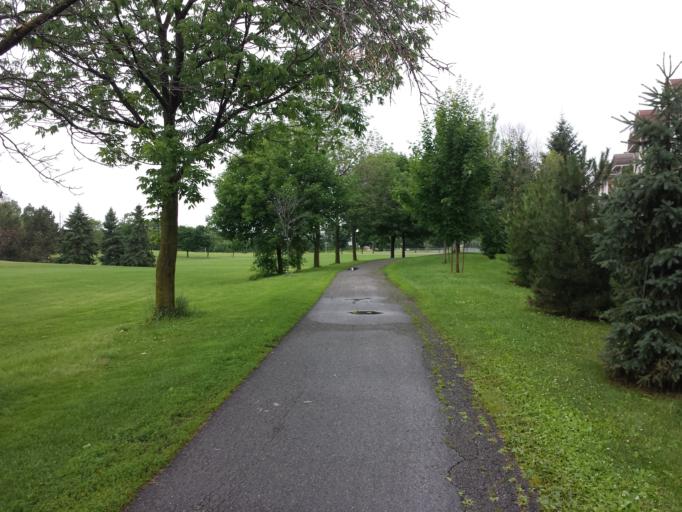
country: CA
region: Ontario
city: Bells Corners
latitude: 45.3420
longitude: -75.7650
